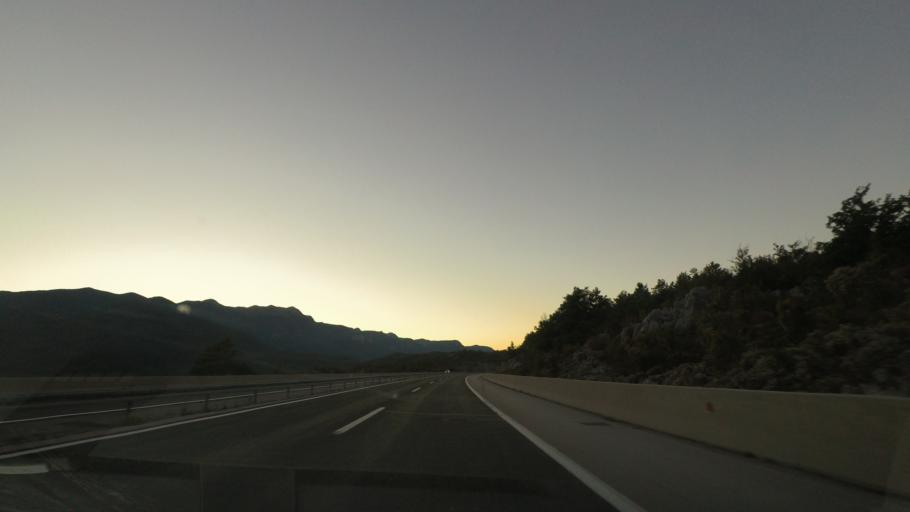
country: HR
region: Zadarska
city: Obrovac
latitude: 44.3331
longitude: 15.6586
